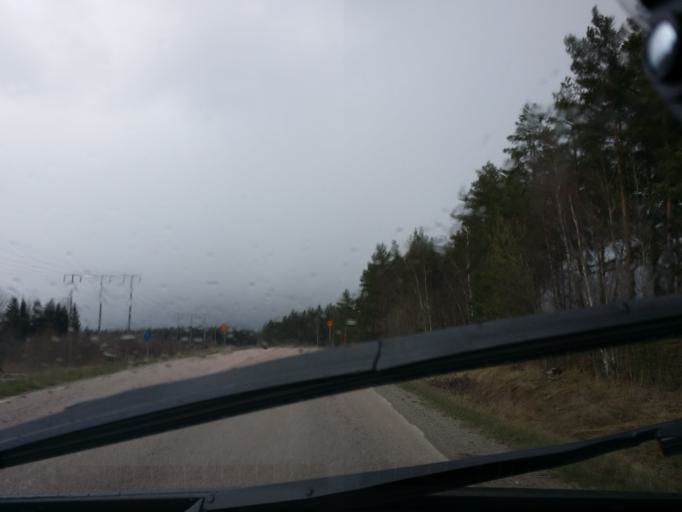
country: SE
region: Uppsala
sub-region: Enkopings Kommun
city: Enkoping
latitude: 59.6396
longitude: 17.1433
